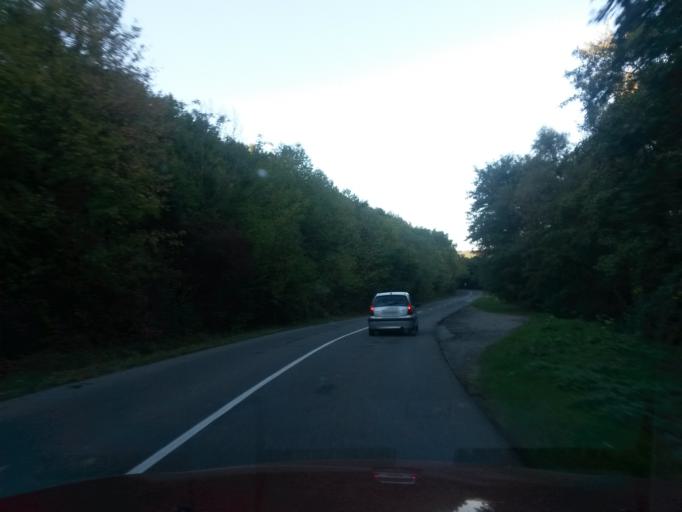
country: SK
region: Kosicky
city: Sobrance
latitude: 48.7847
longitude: 22.2482
